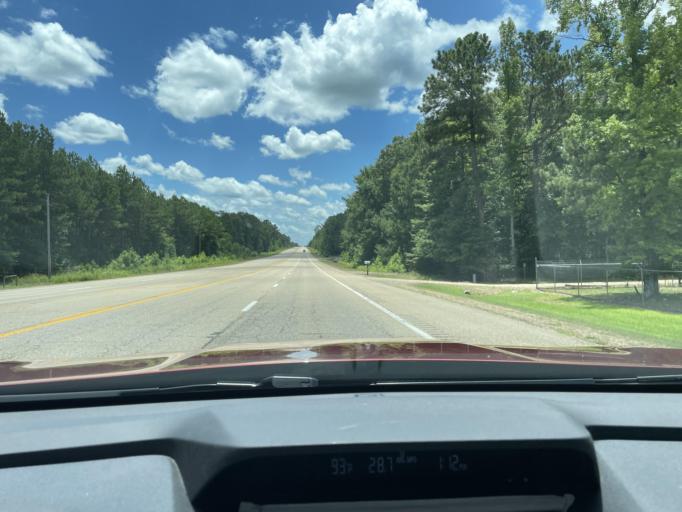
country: US
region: Arkansas
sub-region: Drew County
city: Monticello
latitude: 33.6966
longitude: -91.8068
